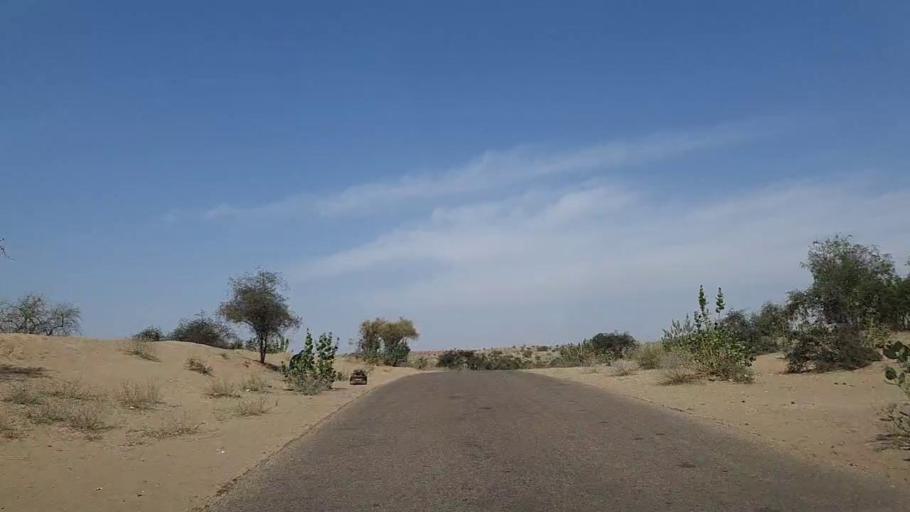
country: PK
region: Sindh
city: Nabisar
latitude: 25.1008
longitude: 69.9930
